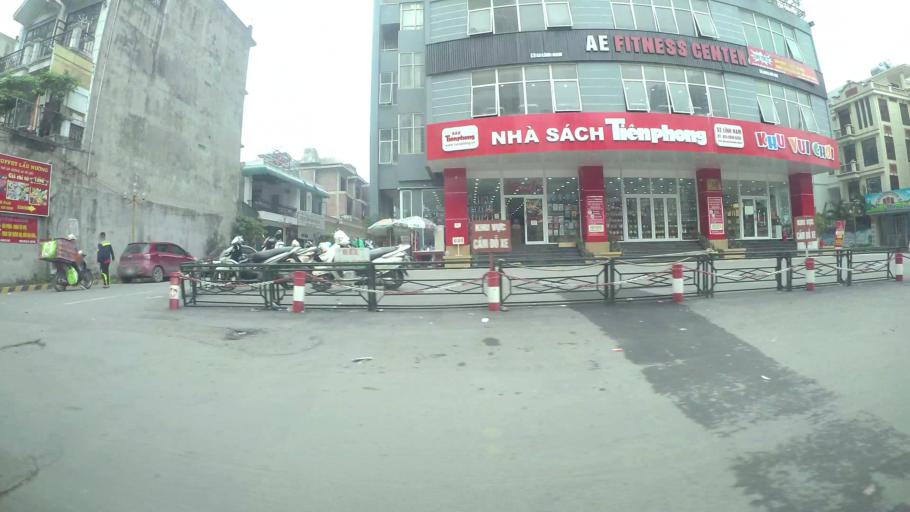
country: VN
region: Ha Noi
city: Hai BaTrung
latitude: 20.9894
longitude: 105.8654
